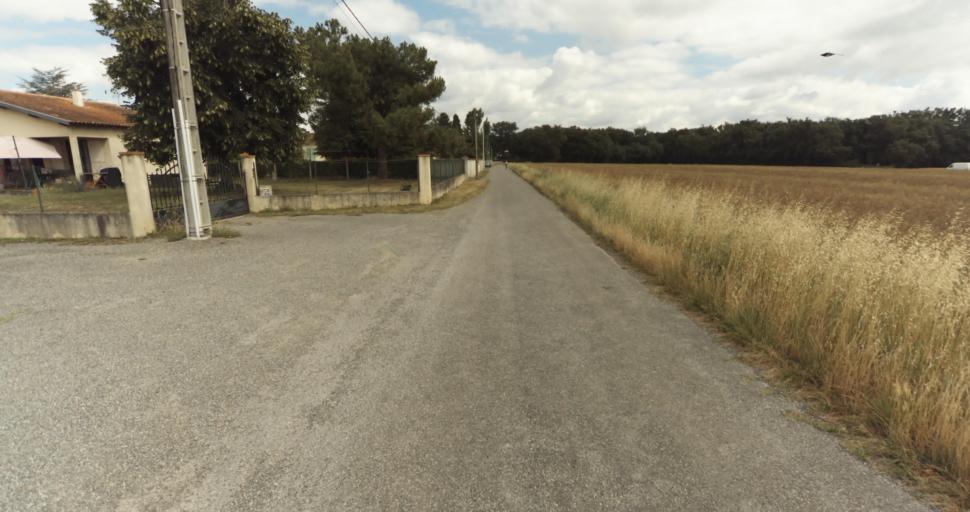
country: FR
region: Midi-Pyrenees
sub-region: Departement de la Haute-Garonne
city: Fontenilles
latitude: 43.5509
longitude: 1.2122
